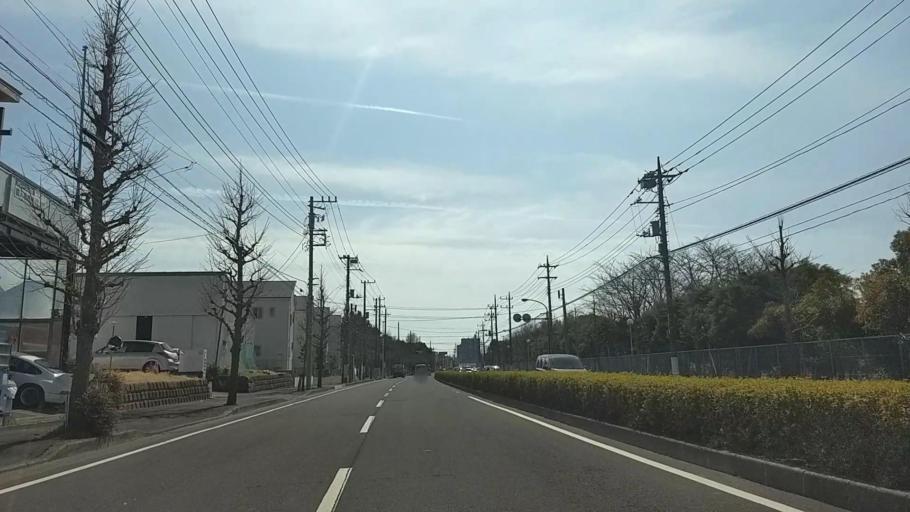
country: JP
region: Kanagawa
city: Fujisawa
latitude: 35.3866
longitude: 139.4572
